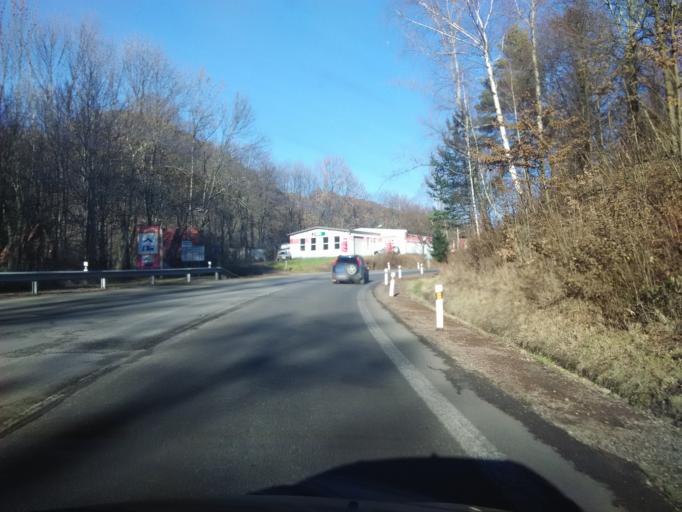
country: SK
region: Banskobystricky
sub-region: Okres Ziar nad Hronom
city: Kremnica
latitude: 48.6923
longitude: 18.9146
